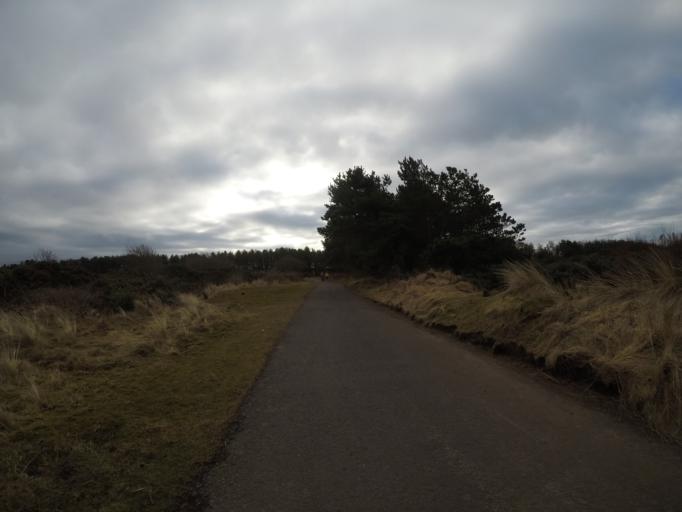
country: GB
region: Scotland
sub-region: North Ayrshire
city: Irvine
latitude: 55.5953
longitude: -4.6736
